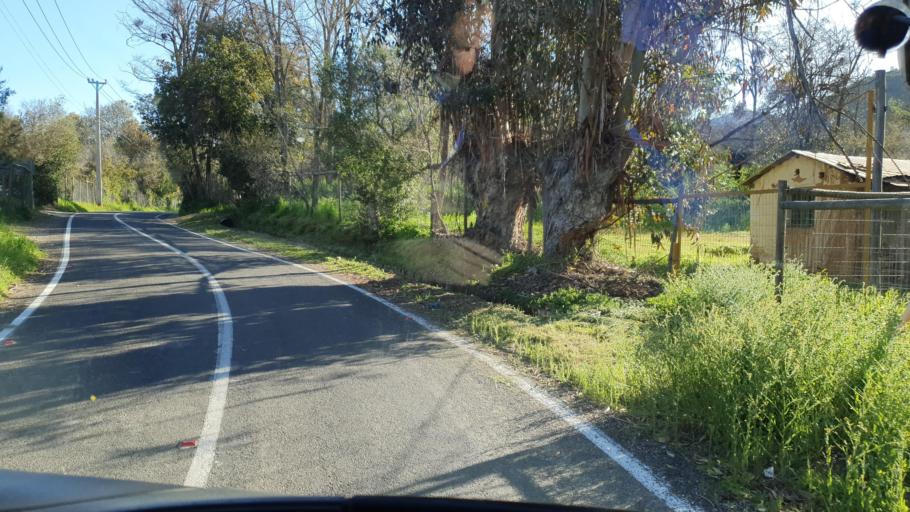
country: CL
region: Valparaiso
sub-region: Provincia de Marga Marga
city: Limache
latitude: -33.1791
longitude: -71.1847
